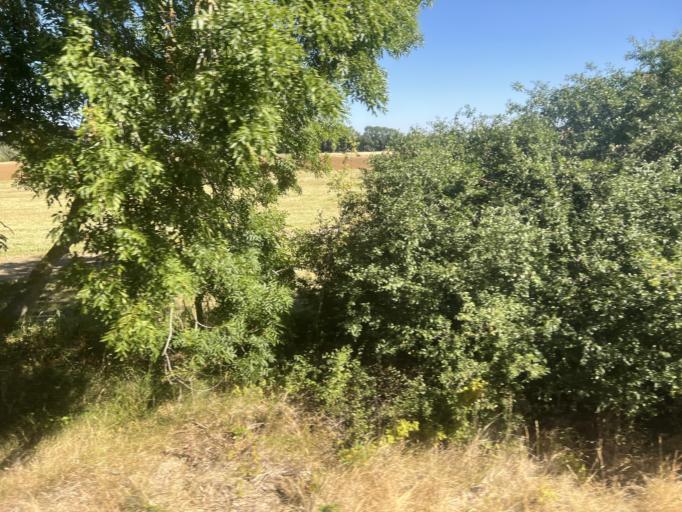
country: GB
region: England
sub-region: Lincolnshire
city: Heckington
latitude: 52.9872
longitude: -0.3456
